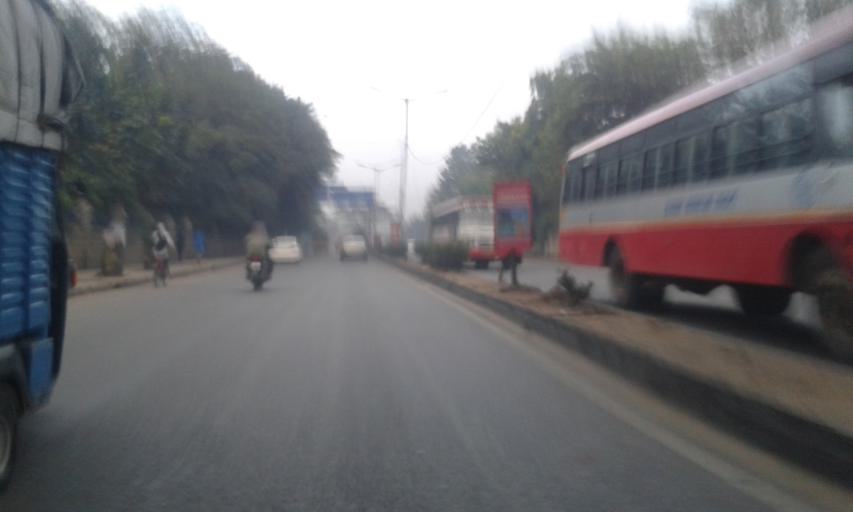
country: IN
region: Karnataka
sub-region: Bangalore Urban
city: Bangalore
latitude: 12.9366
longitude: 77.6054
